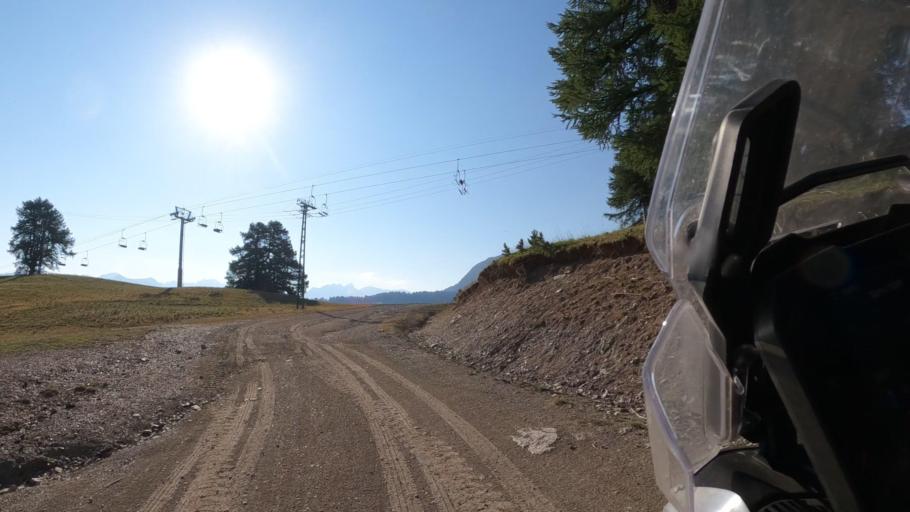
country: FR
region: Provence-Alpes-Cote d'Azur
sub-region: Departement des Hautes-Alpes
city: Guillestre
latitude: 44.6148
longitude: 6.6241
